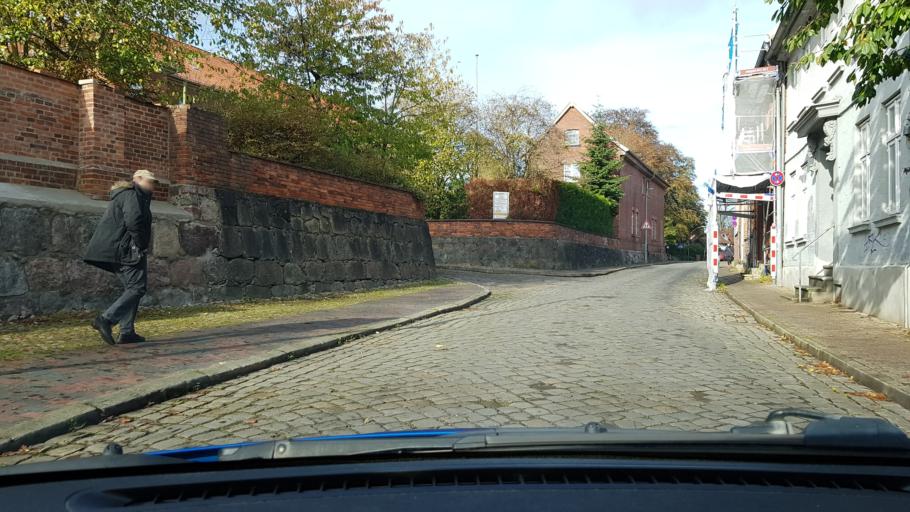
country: DE
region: Lower Saxony
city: Lueneburg
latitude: 53.2485
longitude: 10.3993
